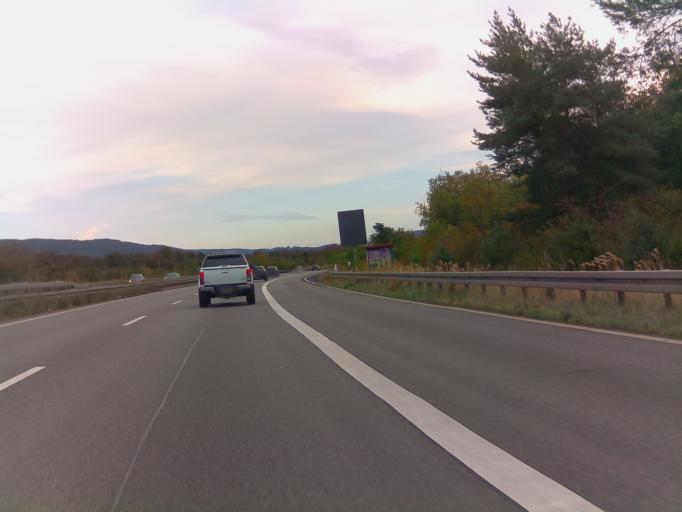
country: DE
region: Hesse
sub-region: Regierungsbezirk Darmstadt
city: Darmstadt
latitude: 49.8348
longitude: 8.6334
